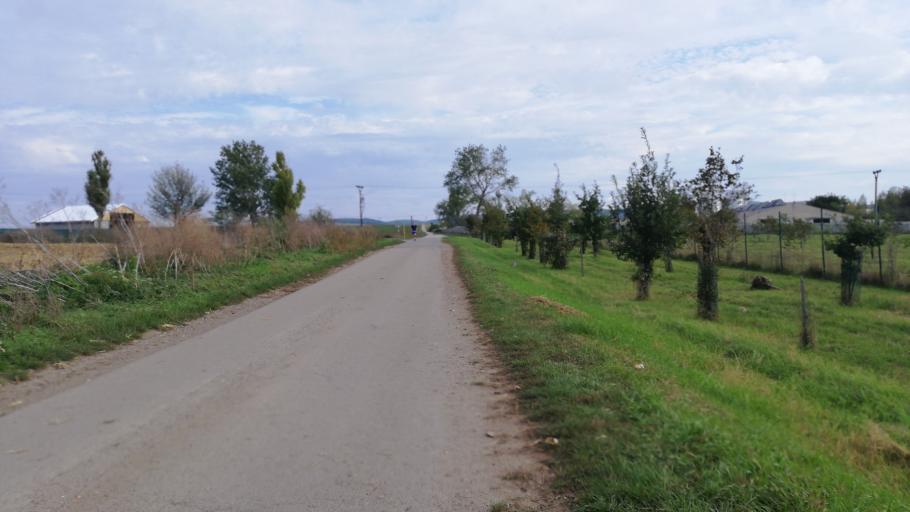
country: CZ
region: South Moravian
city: Sudomerice
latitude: 48.8505
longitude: 17.2494
